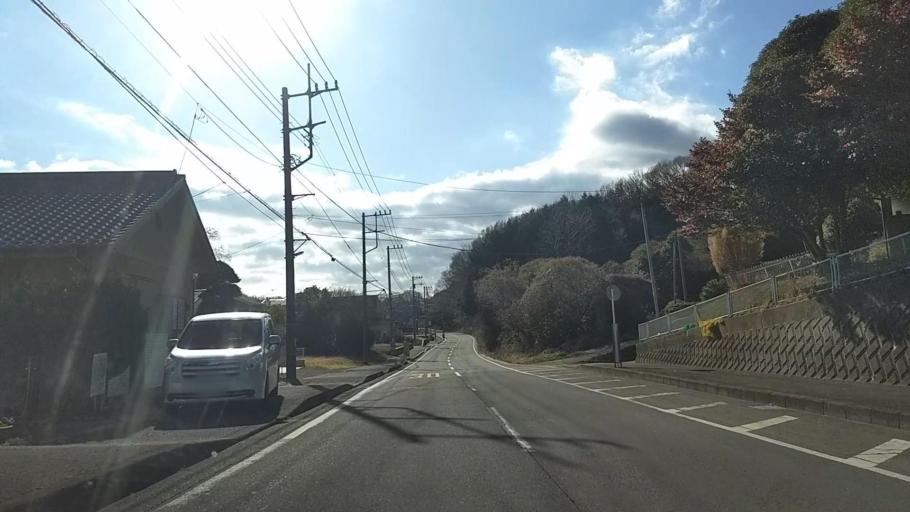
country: JP
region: Kanagawa
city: Atsugi
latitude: 35.4687
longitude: 139.2882
